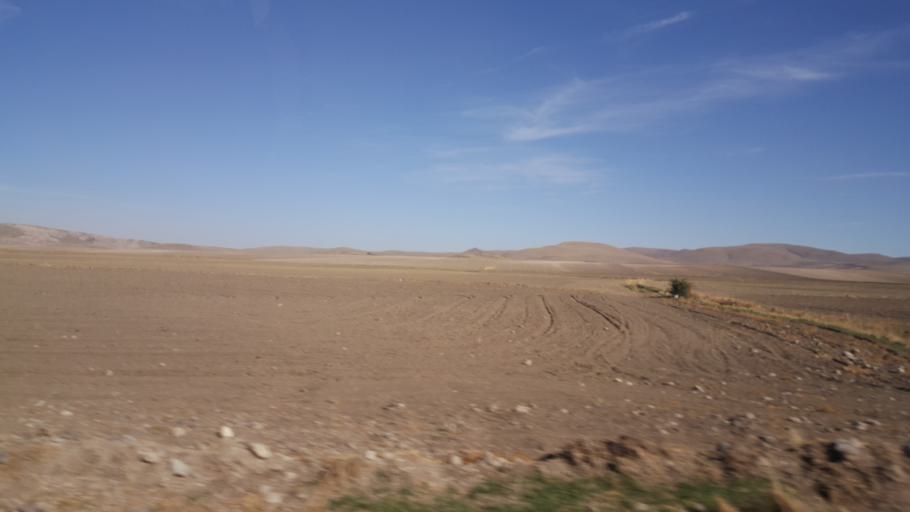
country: TR
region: Ankara
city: Yenice
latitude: 39.3005
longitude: 32.7573
